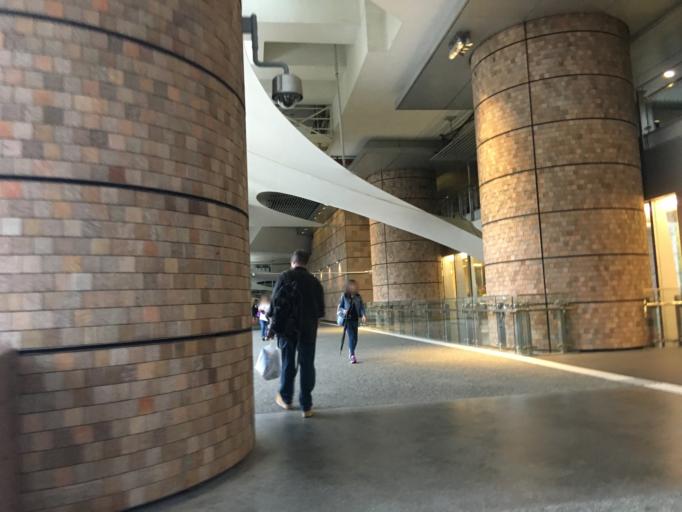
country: HK
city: Tai O
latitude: 22.2914
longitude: 113.9446
